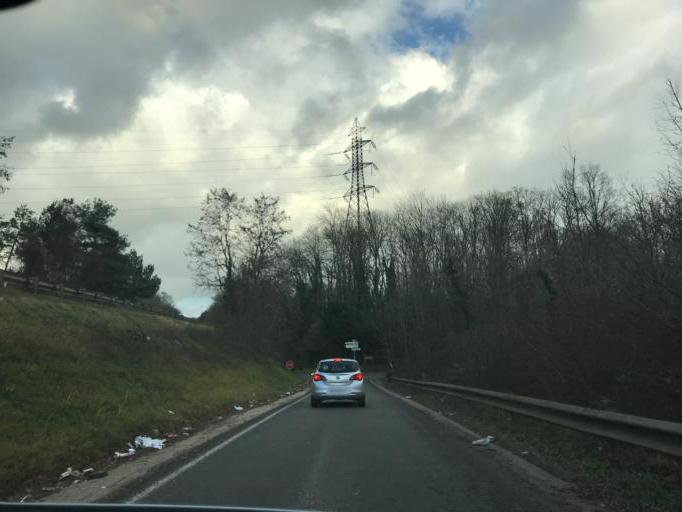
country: FR
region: Ile-de-France
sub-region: Departement de Seine-et-Marne
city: Villevaude
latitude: 48.9028
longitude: 2.6678
